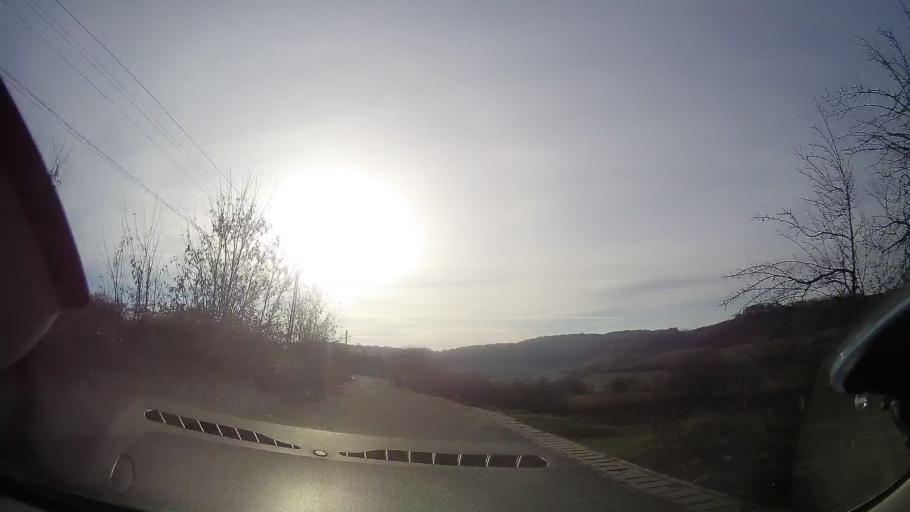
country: RO
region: Bihor
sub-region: Comuna Sarbi
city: Burzuc
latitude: 47.1415
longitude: 22.1841
